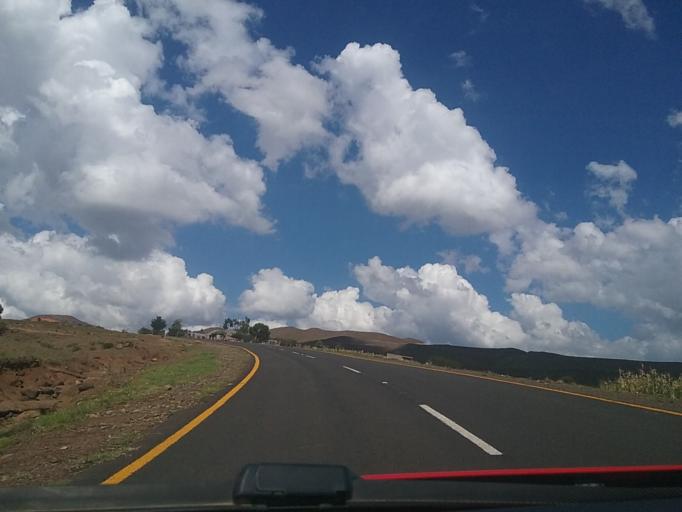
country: LS
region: Berea
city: Teyateyaneng
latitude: -29.2217
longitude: 27.8578
